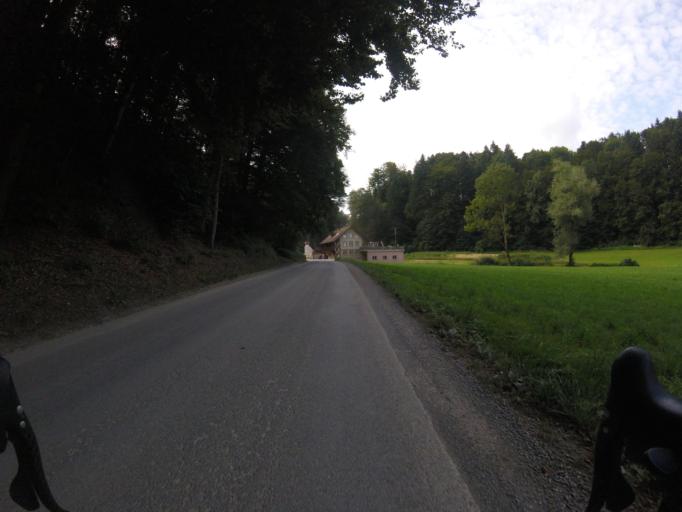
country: CH
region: Bern
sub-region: Emmental District
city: Oberburg
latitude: 47.0317
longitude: 7.6095
